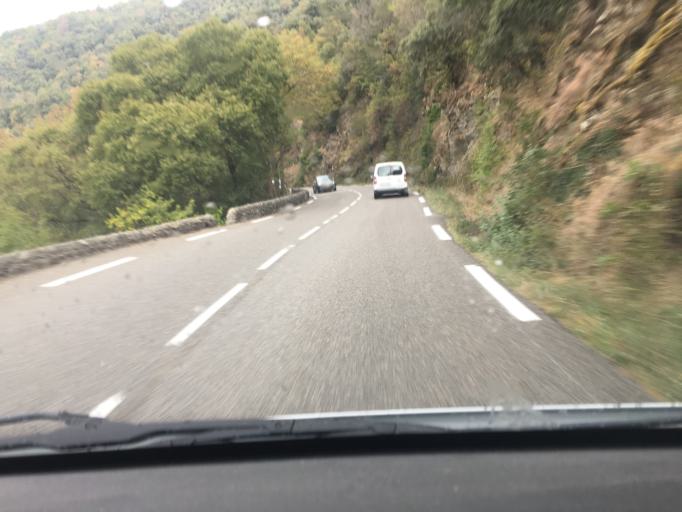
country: FR
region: Rhone-Alpes
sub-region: Departement de l'Ardeche
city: Saint-Jean-de-Muzols
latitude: 45.0592
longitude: 4.7856
